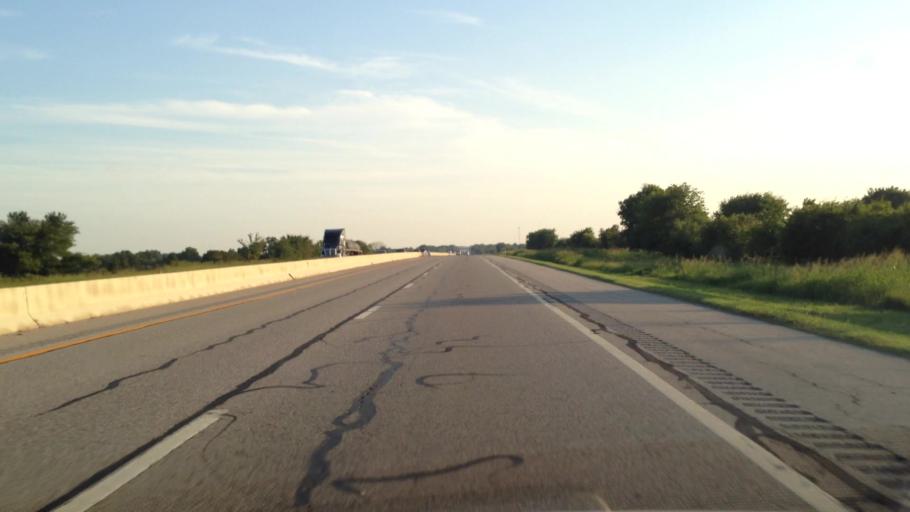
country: US
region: Oklahoma
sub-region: Ottawa County
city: Fairland
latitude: 36.7990
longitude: -94.8813
